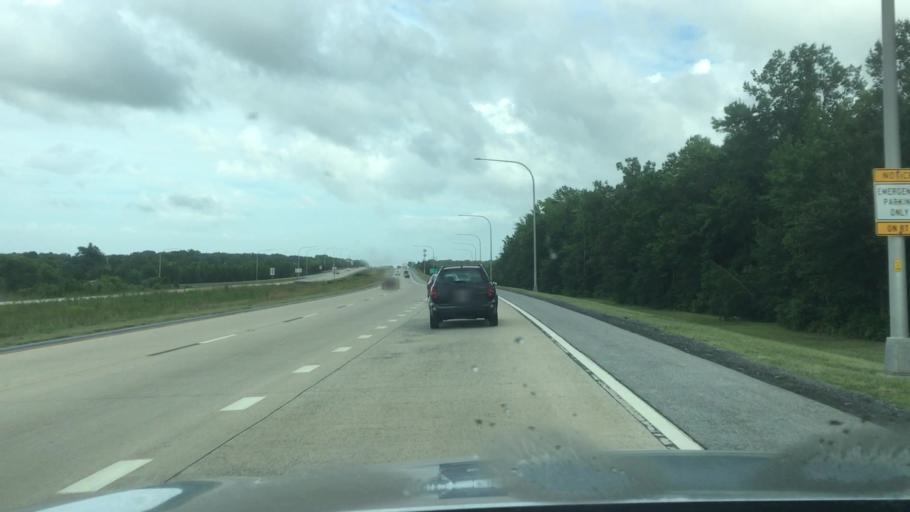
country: US
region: Delaware
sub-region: Kent County
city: Clayton
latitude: 39.3344
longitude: -75.6333
